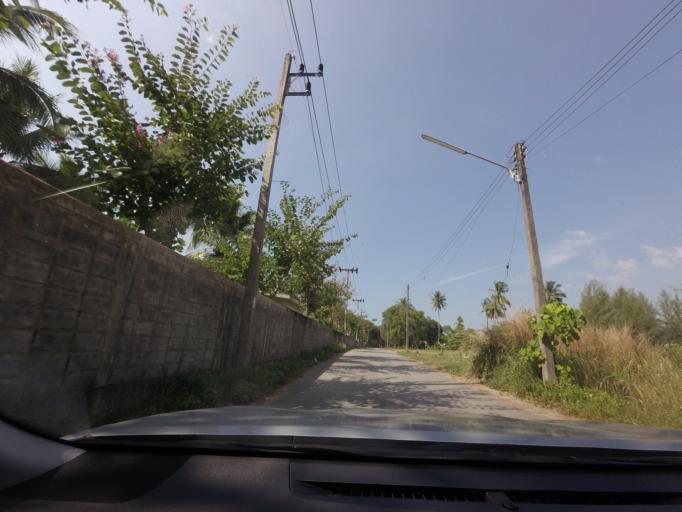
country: TH
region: Phangnga
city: Ban Khao Lak
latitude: 8.6645
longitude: 98.2496
